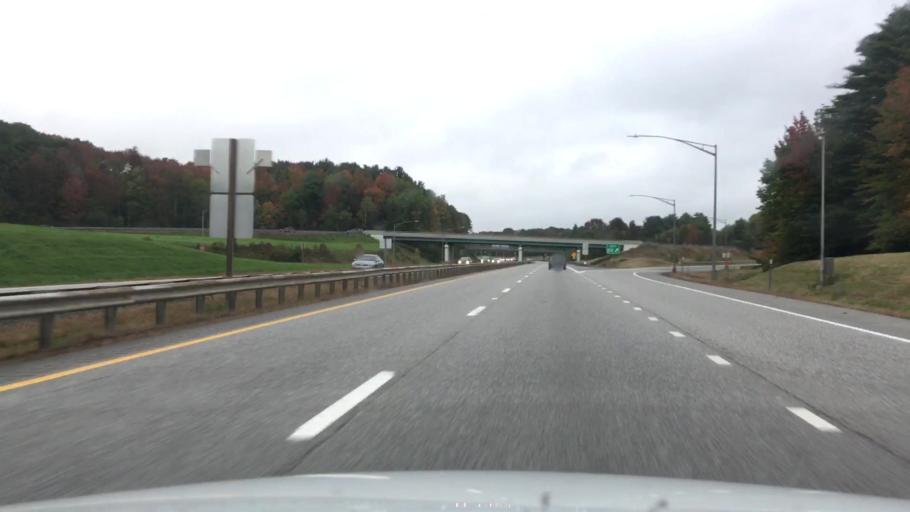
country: US
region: Maine
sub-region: Cumberland County
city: Falmouth
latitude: 43.7300
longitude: -70.3028
